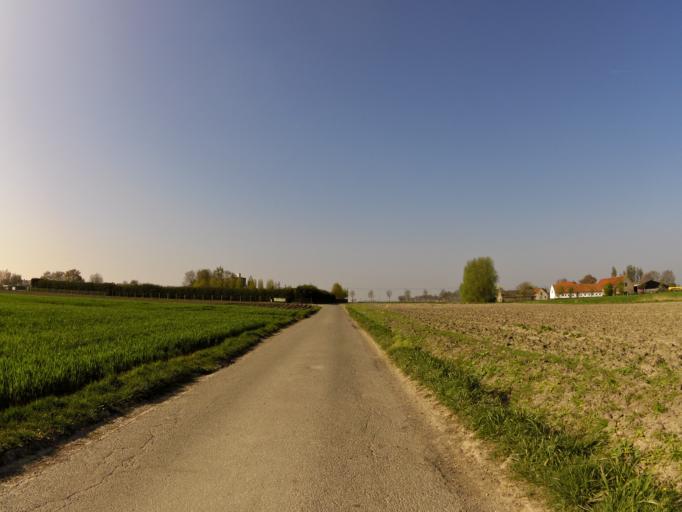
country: BE
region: Flanders
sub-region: Provincie West-Vlaanderen
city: Gistel
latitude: 51.1369
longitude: 2.9296
